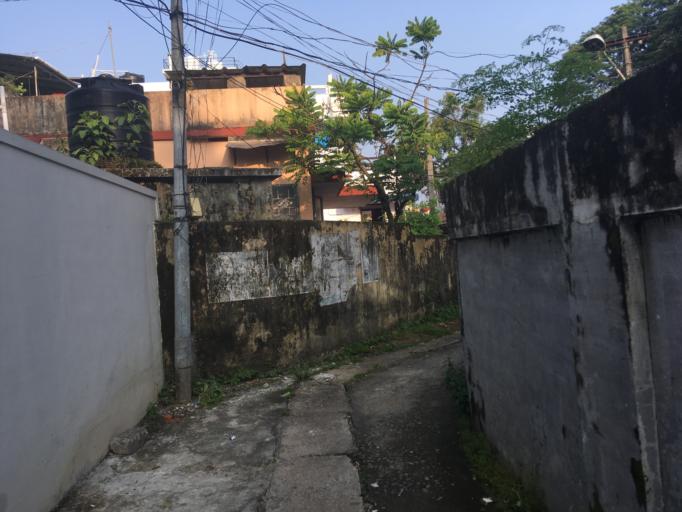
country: IN
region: Kerala
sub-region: Ernakulam
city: Cochin
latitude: 9.9578
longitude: 76.2398
